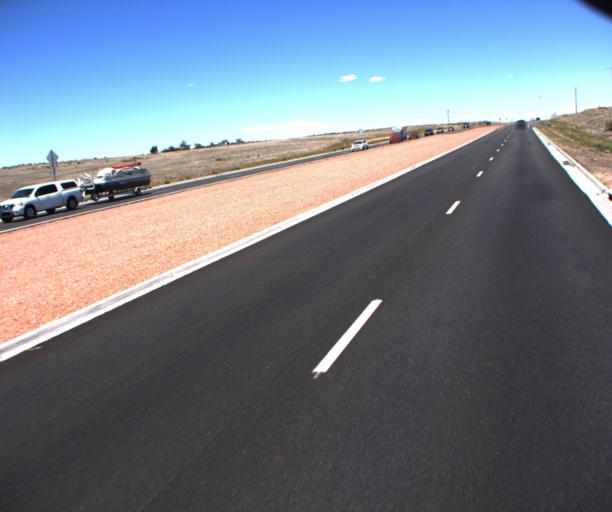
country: US
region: Arizona
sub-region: Yavapai County
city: Chino Valley
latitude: 34.6553
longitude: -112.4356
